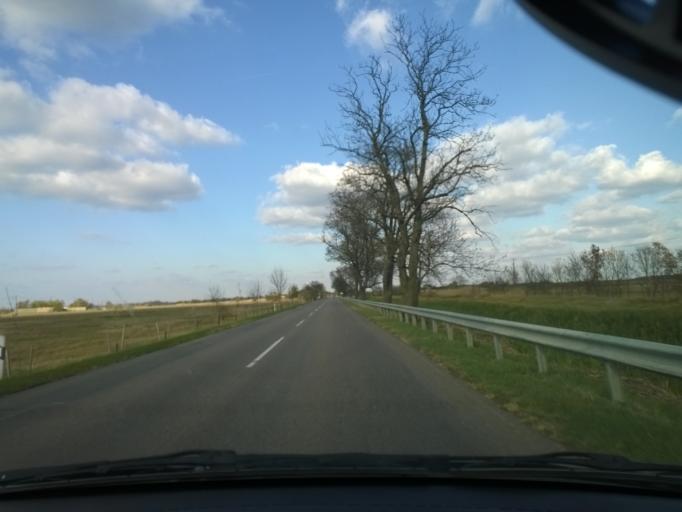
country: HU
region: Csongrad
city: Szegvar
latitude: 46.5310
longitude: 20.3133
